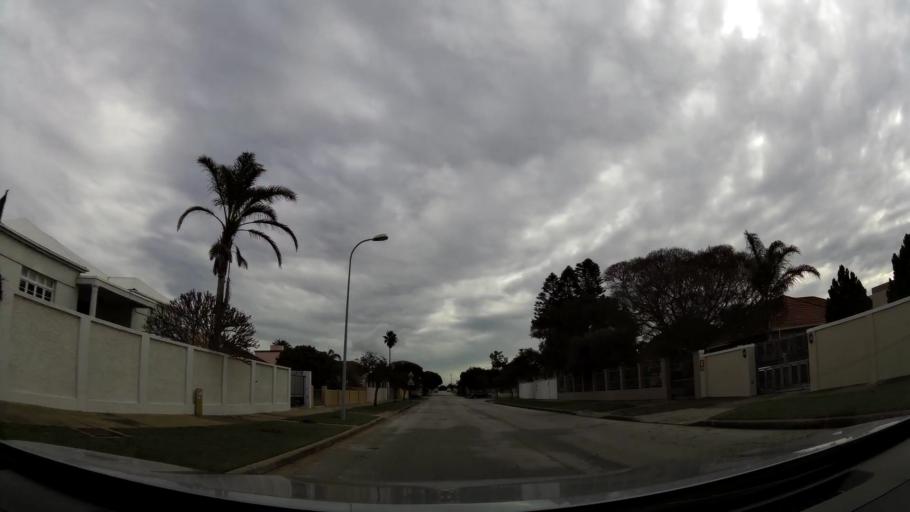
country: ZA
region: Eastern Cape
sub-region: Nelson Mandela Bay Metropolitan Municipality
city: Port Elizabeth
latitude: -33.9546
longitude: 25.6008
